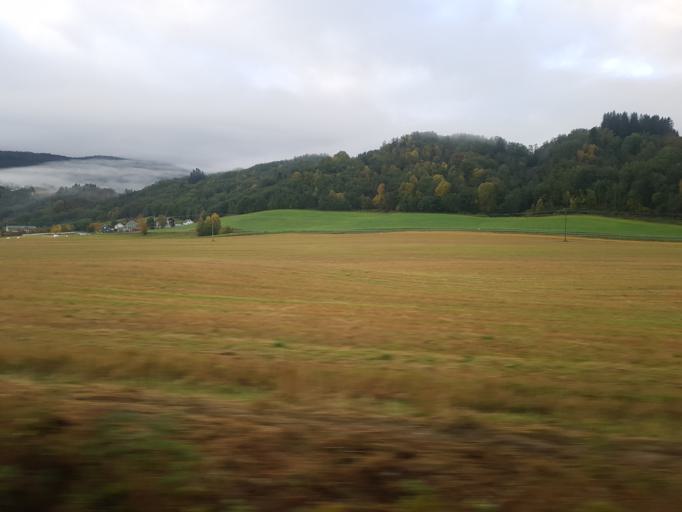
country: NO
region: Sor-Trondelag
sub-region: Melhus
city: Melhus
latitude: 63.2968
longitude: 10.2869
